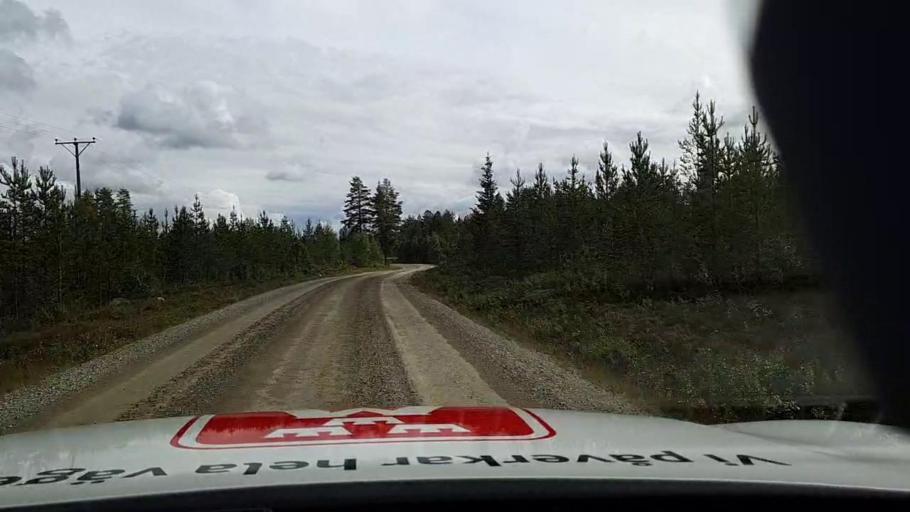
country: SE
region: Jaemtland
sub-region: Are Kommun
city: Jarpen
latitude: 62.5061
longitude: 13.4979
